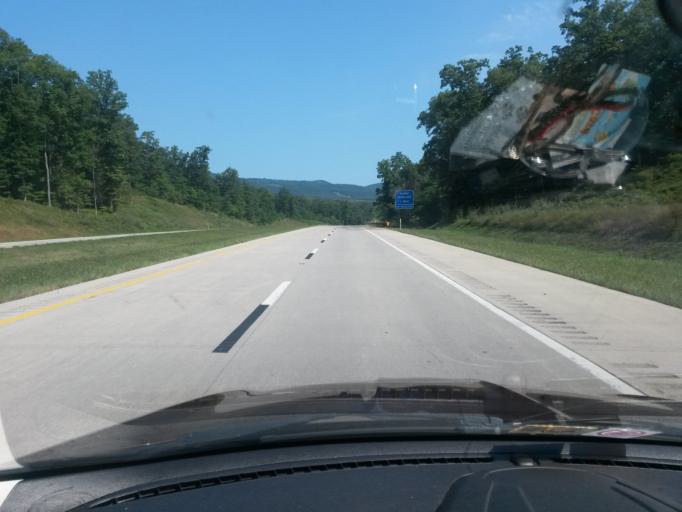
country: US
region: West Virginia
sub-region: Hardy County
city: Moorefield
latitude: 39.1245
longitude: -78.9817
